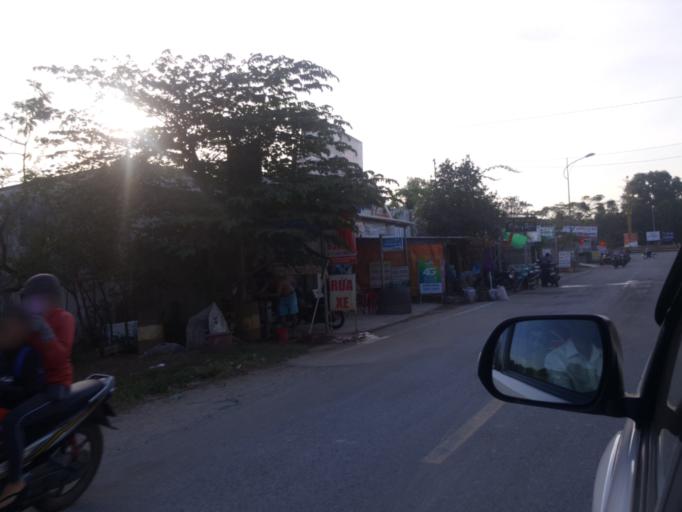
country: VN
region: Kien Giang
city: Duong GJong
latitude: 10.1507
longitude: 104.0335
